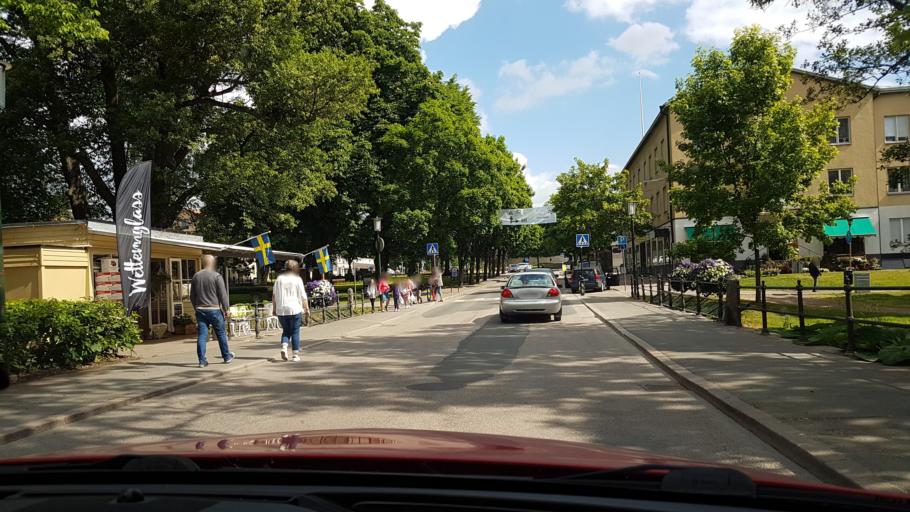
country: SE
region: Vaestra Goetaland
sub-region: Hjo Kommun
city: Hjo
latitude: 58.3024
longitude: 14.2903
